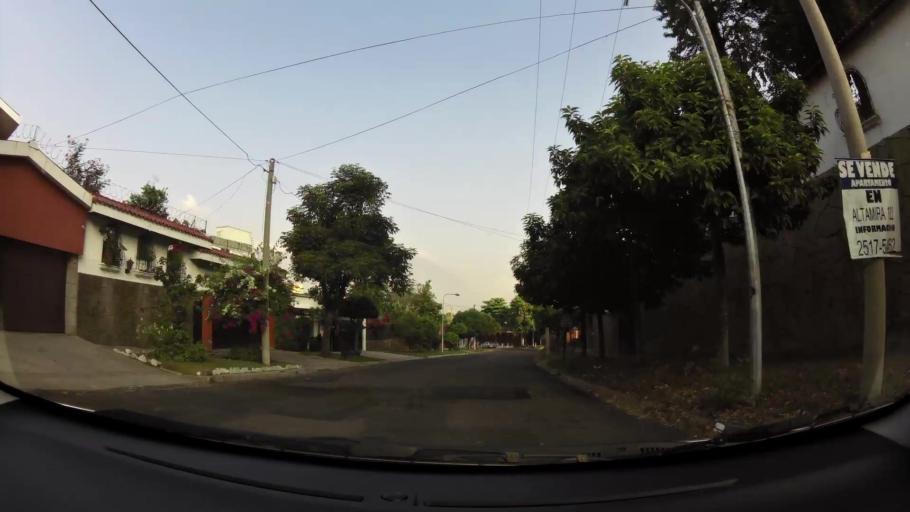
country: SV
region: San Salvador
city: San Salvador
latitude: 13.6807
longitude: -89.2182
